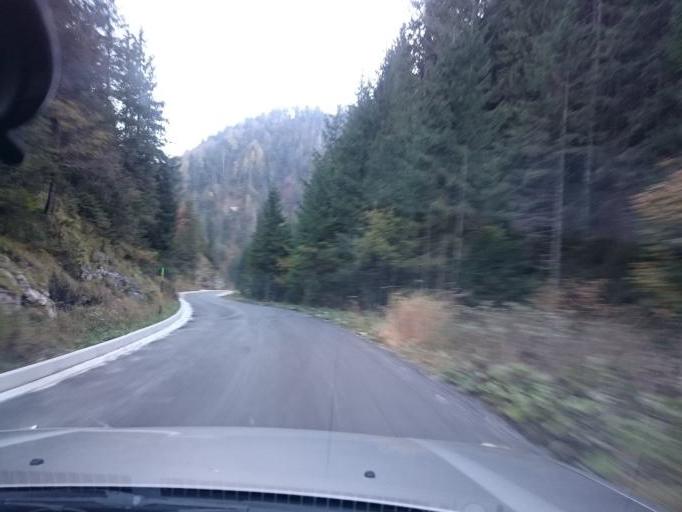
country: IT
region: Veneto
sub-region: Provincia di Vicenza
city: Roana
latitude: 45.9529
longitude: 11.4295
